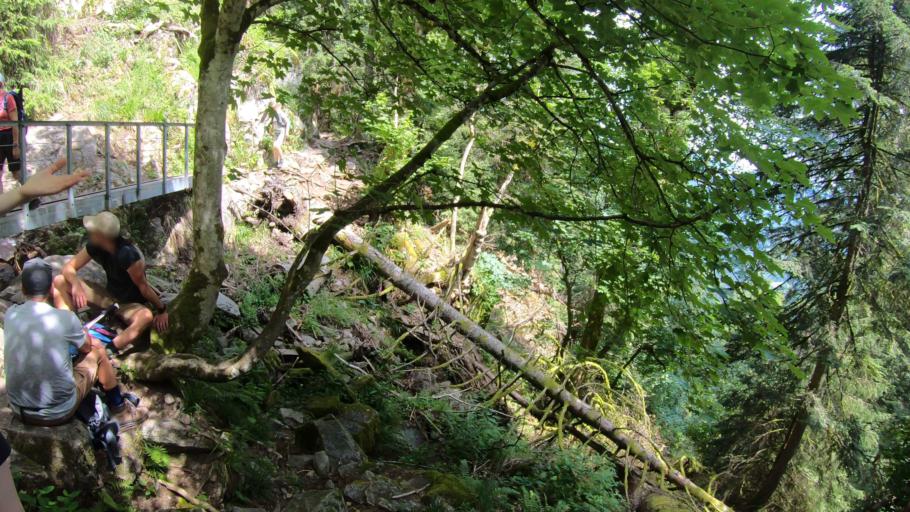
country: FR
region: Alsace
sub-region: Departement du Haut-Rhin
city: Metzeral
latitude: 48.0504
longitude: 7.0306
